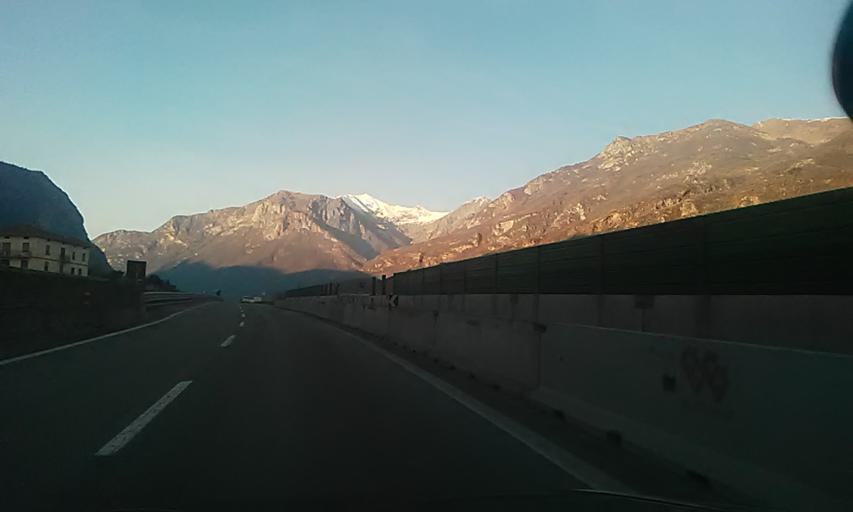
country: IT
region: Piedmont
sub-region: Provincia di Torino
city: Tavagnasco
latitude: 45.5469
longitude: 7.8240
